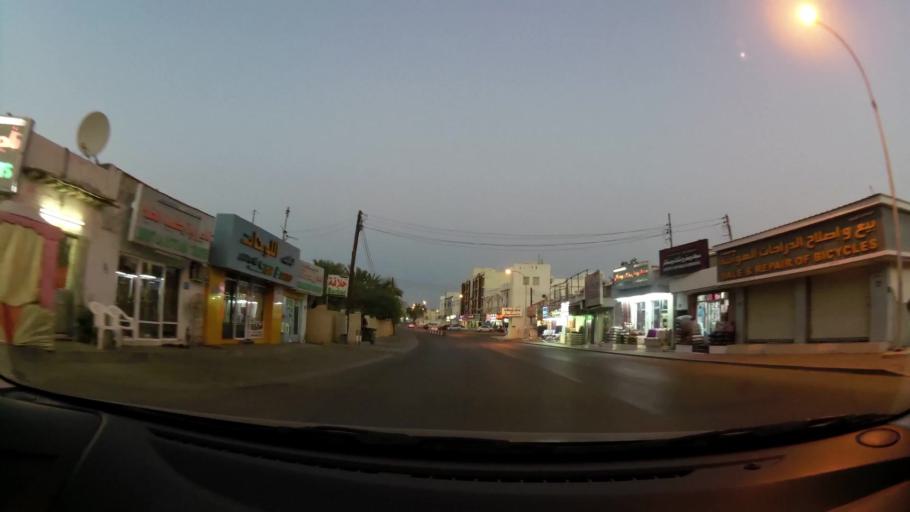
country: OM
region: Muhafazat Masqat
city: As Sib al Jadidah
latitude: 23.6820
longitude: 58.1811
